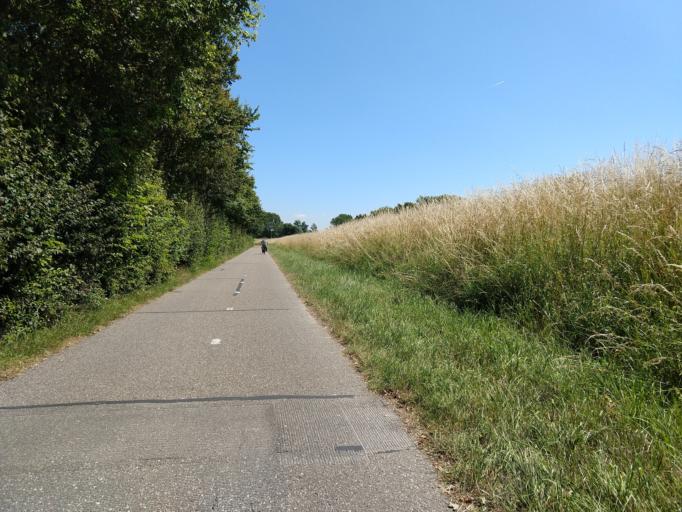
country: NL
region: Zeeland
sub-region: Gemeente Veere
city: Veere
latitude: 51.5583
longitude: 3.6458
